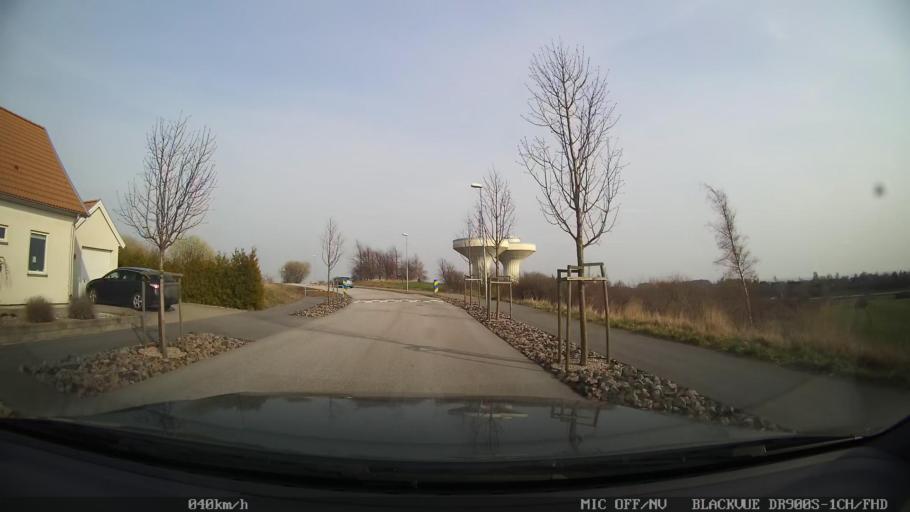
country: SE
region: Skane
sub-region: Ystads Kommun
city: Ystad
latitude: 55.4433
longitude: 13.7996
